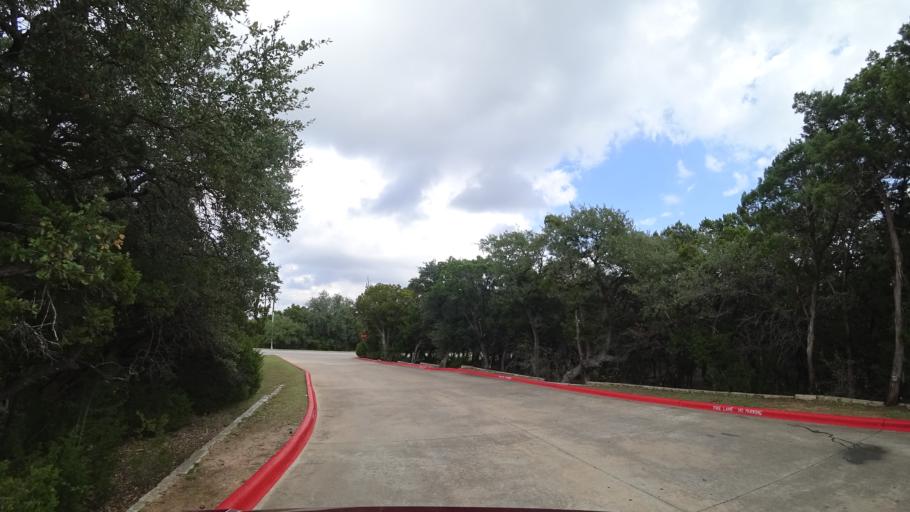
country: US
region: Texas
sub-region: Williamson County
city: Anderson Mill
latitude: 30.4211
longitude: -97.8439
